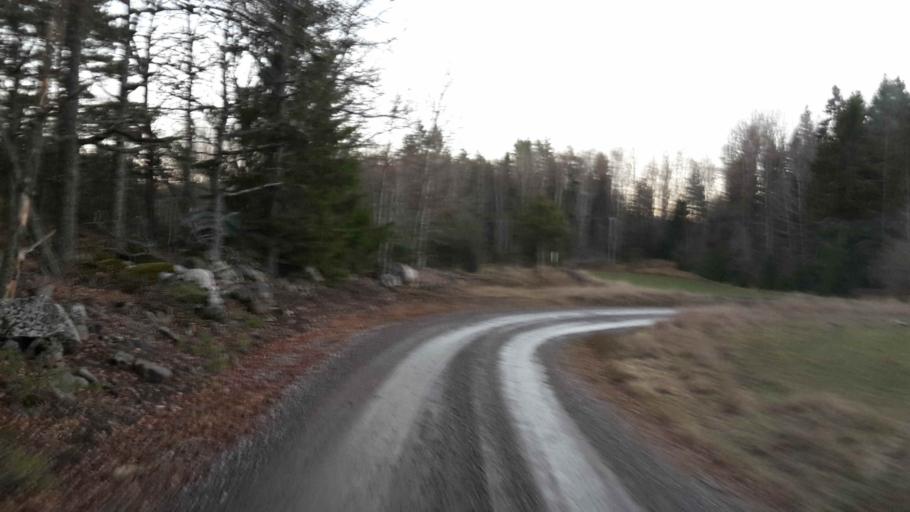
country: SE
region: OEstergoetland
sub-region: Atvidabergs Kommun
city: Atvidaberg
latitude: 58.2666
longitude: 16.0732
